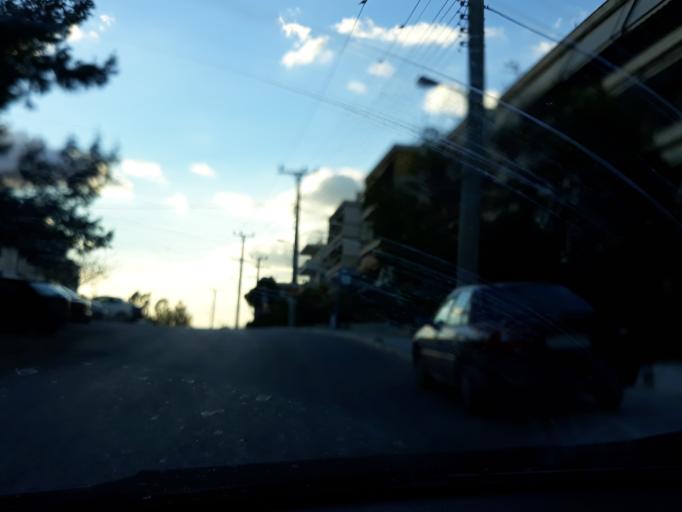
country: GR
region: Attica
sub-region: Nomarchia Anatolikis Attikis
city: Acharnes
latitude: 38.0811
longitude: 23.7228
